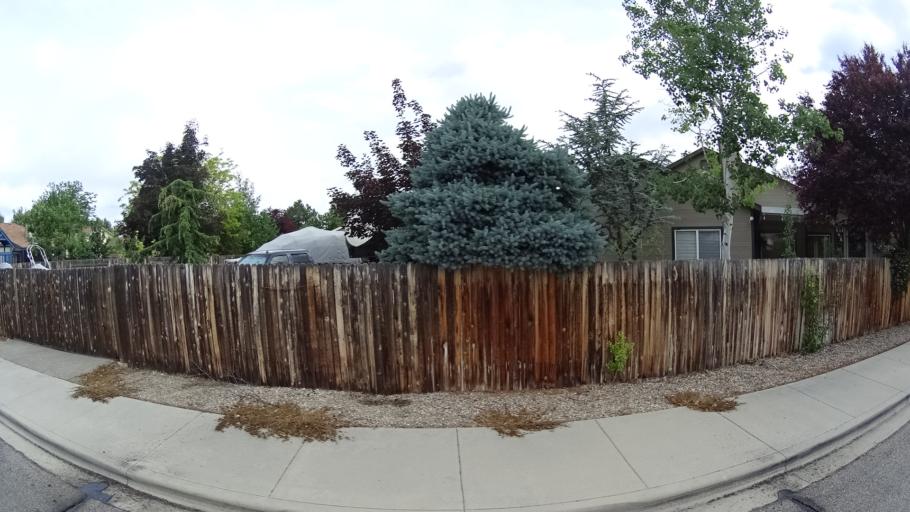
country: US
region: Idaho
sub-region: Ada County
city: Meridian
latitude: 43.5860
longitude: -116.3960
